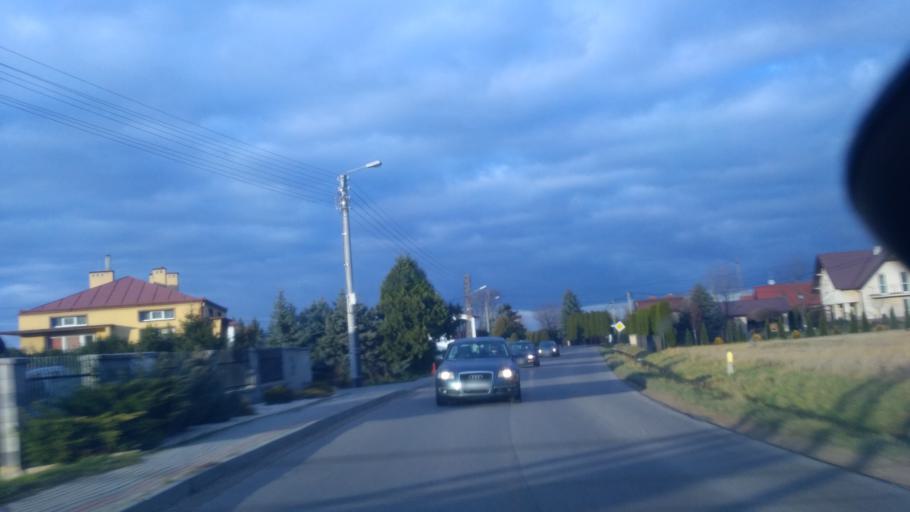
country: PL
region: Subcarpathian Voivodeship
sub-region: Powiat rzeszowski
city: Krasne
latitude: 50.0572
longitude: 22.1199
